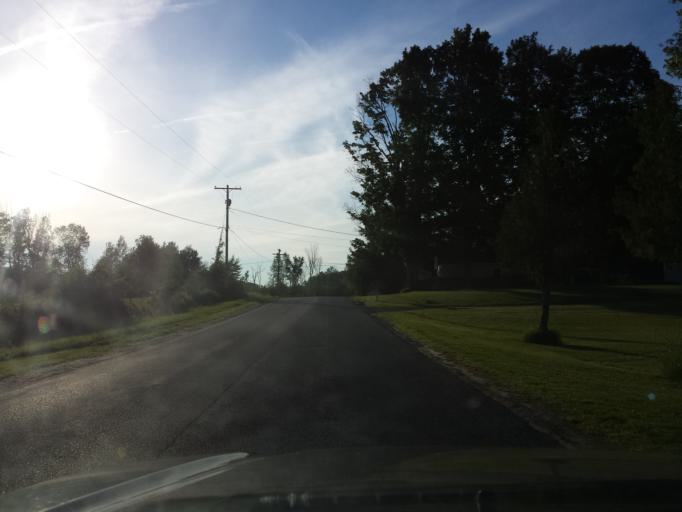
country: US
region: New York
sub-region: St. Lawrence County
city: Norwood
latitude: 44.7229
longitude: -74.9502
